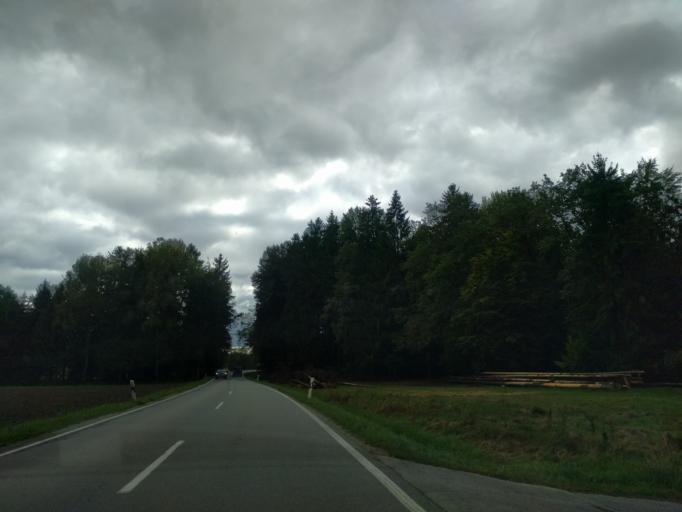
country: DE
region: Bavaria
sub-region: Lower Bavaria
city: Auerbach
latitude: 48.8150
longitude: 13.0911
